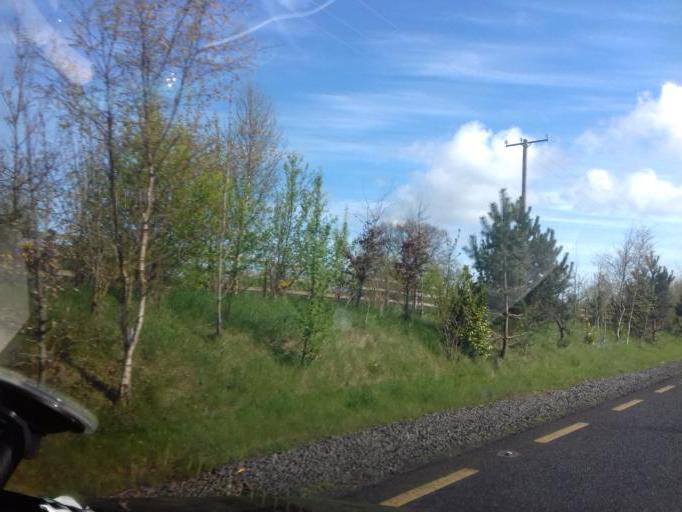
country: IE
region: Leinster
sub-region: An Mhi
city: Kells
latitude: 53.7112
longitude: -6.8536
